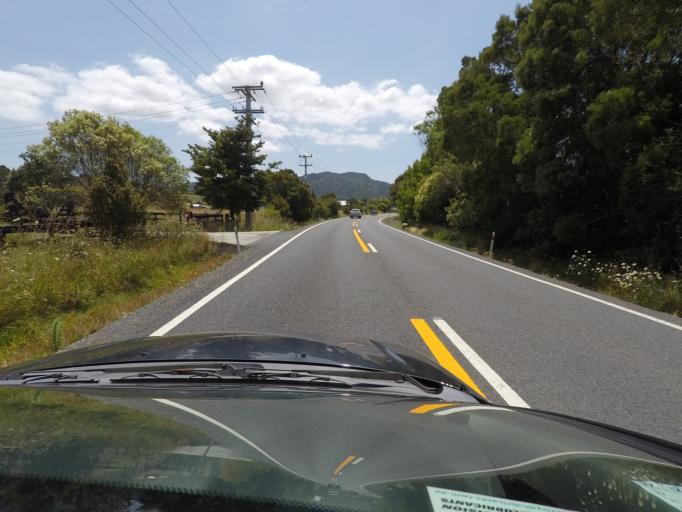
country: NZ
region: Auckland
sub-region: Auckland
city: Warkworth
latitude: -36.3312
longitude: 174.7327
